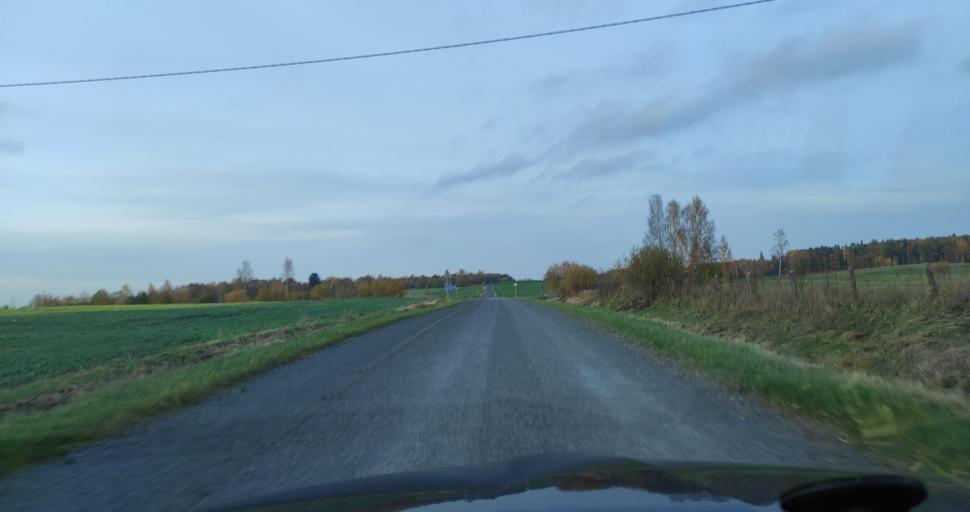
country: LV
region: Aizpute
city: Aizpute
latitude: 56.6980
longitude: 21.7960
